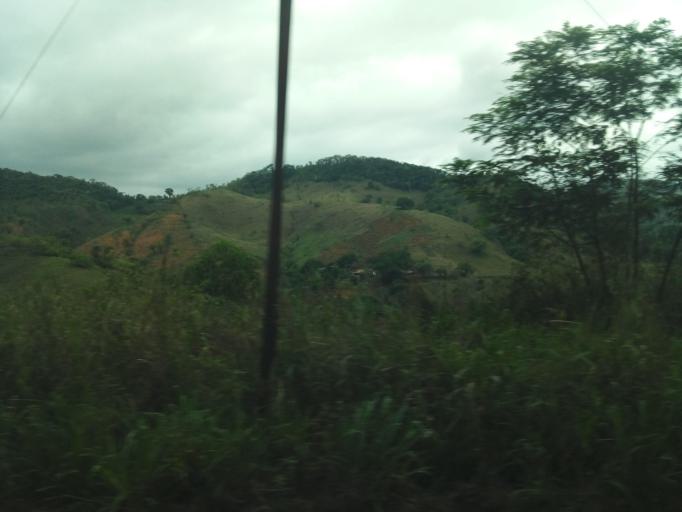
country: BR
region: Minas Gerais
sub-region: Nova Era
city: Nova Era
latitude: -19.6815
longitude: -42.9121
